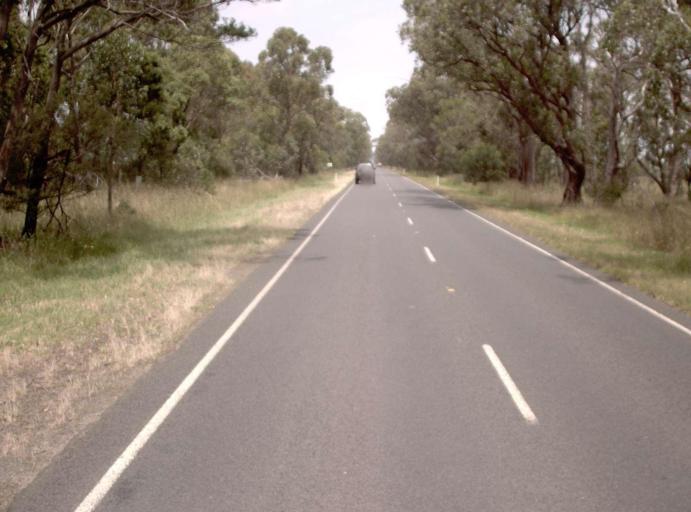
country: AU
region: Victoria
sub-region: Latrobe
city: Traralgon
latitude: -38.4841
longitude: 146.7147
